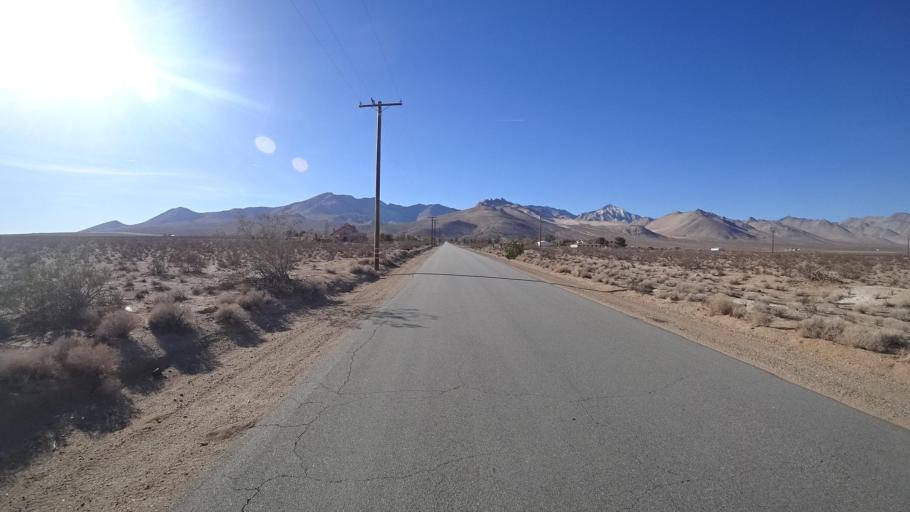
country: US
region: California
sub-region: Kern County
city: Inyokern
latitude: 35.6813
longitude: -117.8469
